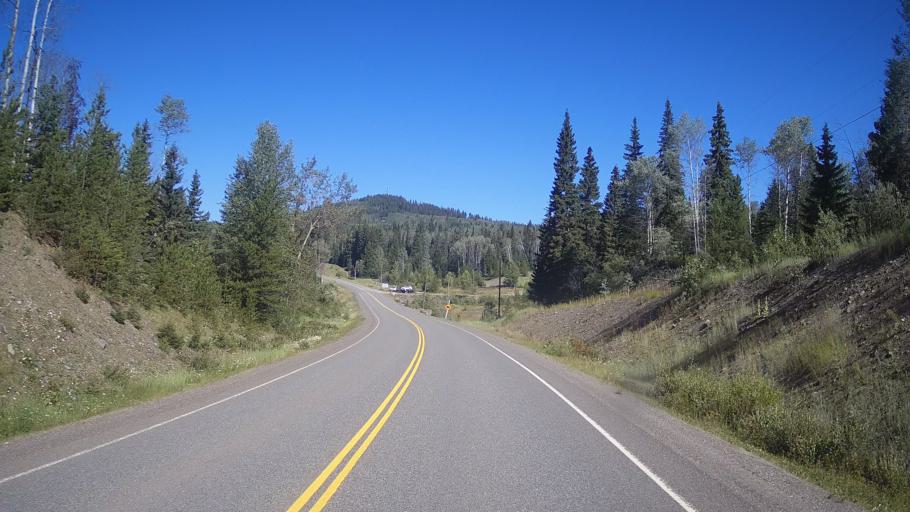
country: CA
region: British Columbia
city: Kamloops
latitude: 51.4897
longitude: -120.5657
